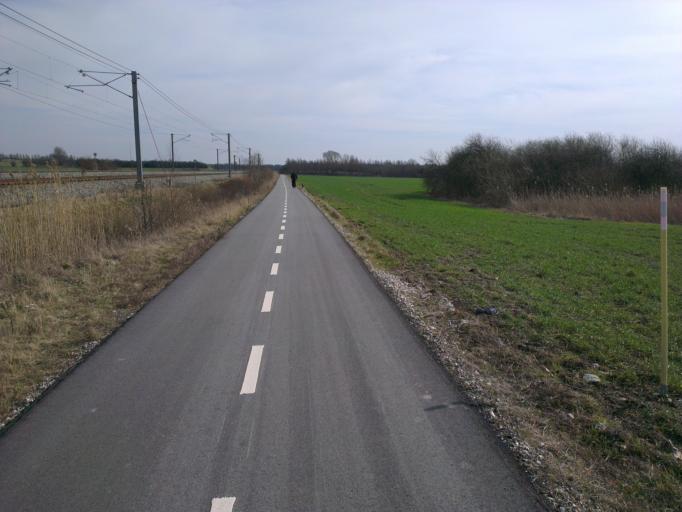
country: DK
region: Capital Region
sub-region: Frederikssund Kommune
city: Frederikssund
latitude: 55.8159
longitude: 12.0905
